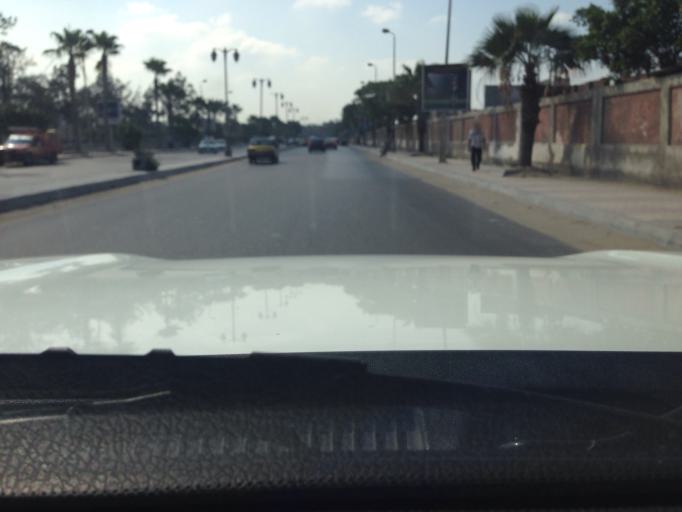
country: EG
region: Alexandria
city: Alexandria
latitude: 31.2066
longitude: 29.9668
